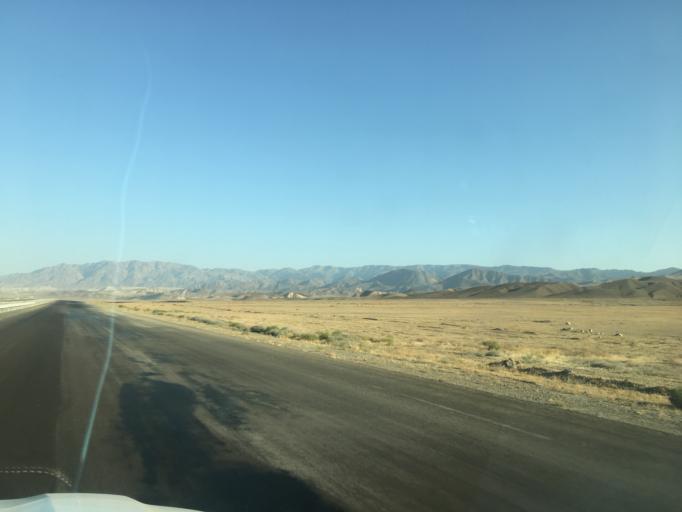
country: TM
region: Ahal
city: Baharly
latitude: 38.6693
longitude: 56.8679
